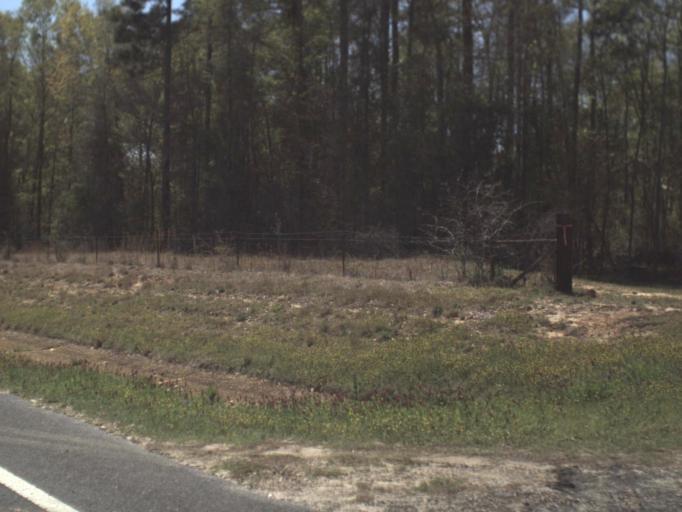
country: US
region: Florida
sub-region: Walton County
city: DeFuniak Springs
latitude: 30.8373
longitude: -85.9521
